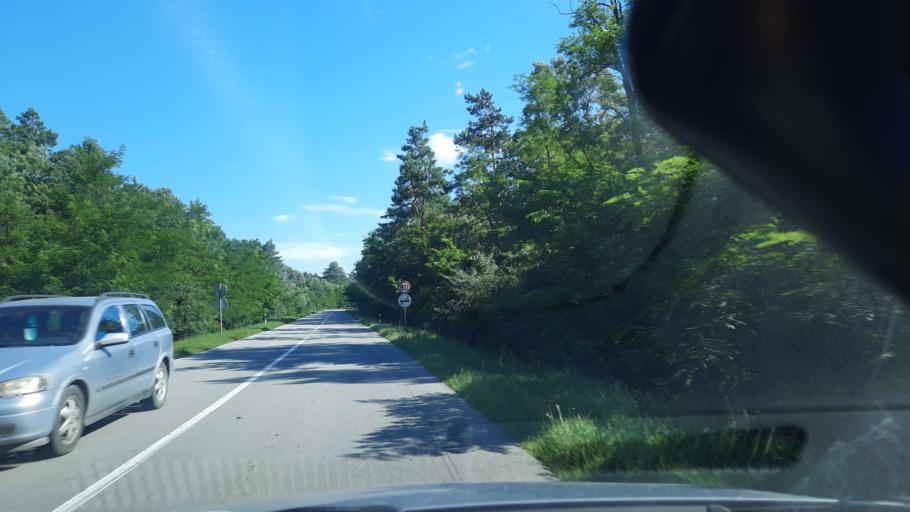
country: RO
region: Caras-Severin
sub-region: Comuna Socol
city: Socol
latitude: 44.8155
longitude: 21.2302
